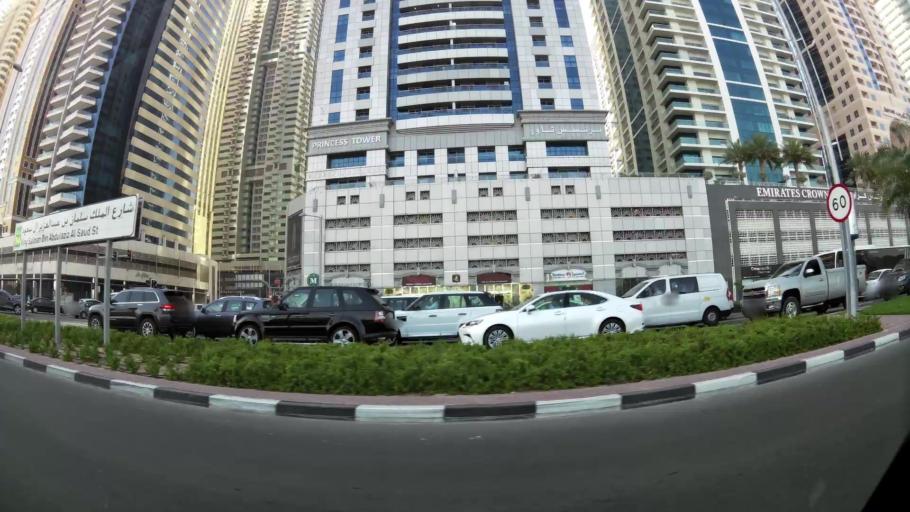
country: AE
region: Dubai
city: Dubai
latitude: 25.0893
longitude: 55.1463
